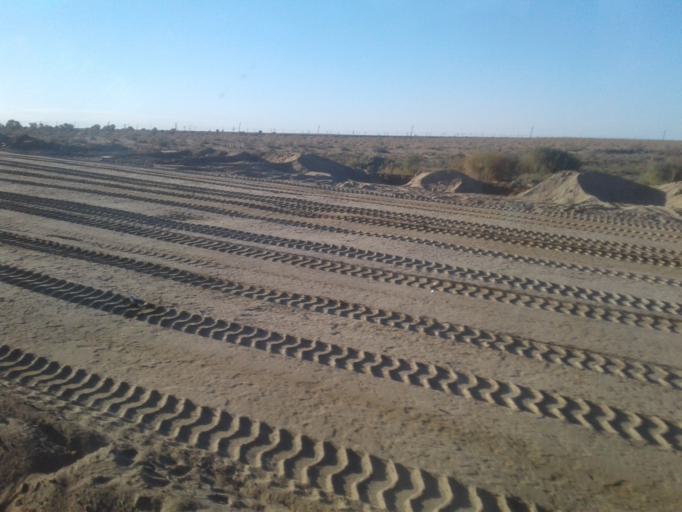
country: TM
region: Mary
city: Seydi
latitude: 39.4413
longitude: 62.8671
